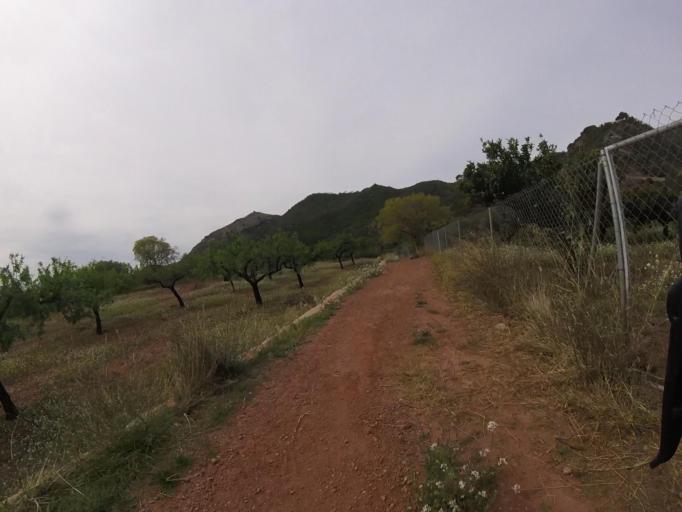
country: ES
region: Valencia
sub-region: Provincia de Castello
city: Benicassim
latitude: 40.0747
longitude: 0.0362
